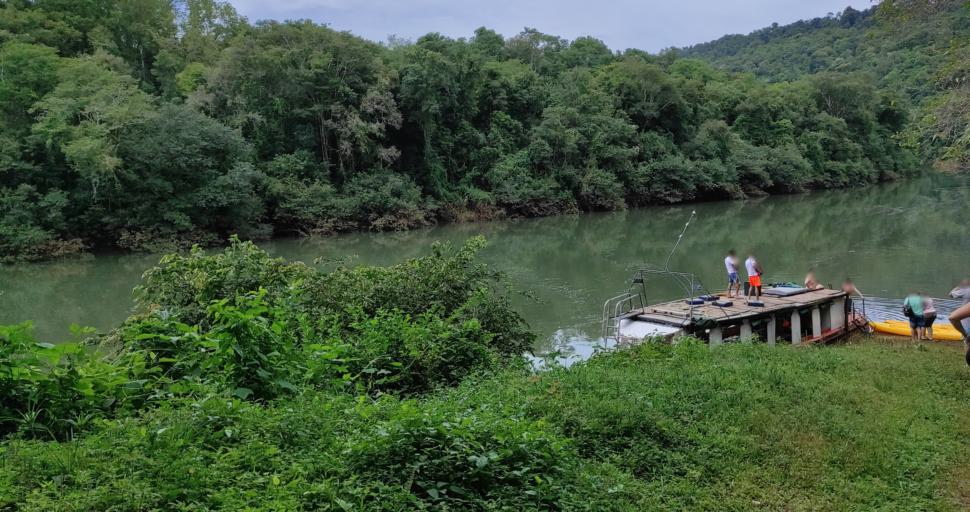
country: AR
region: Misiones
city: El Soberbio
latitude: -27.2765
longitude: -54.2208
